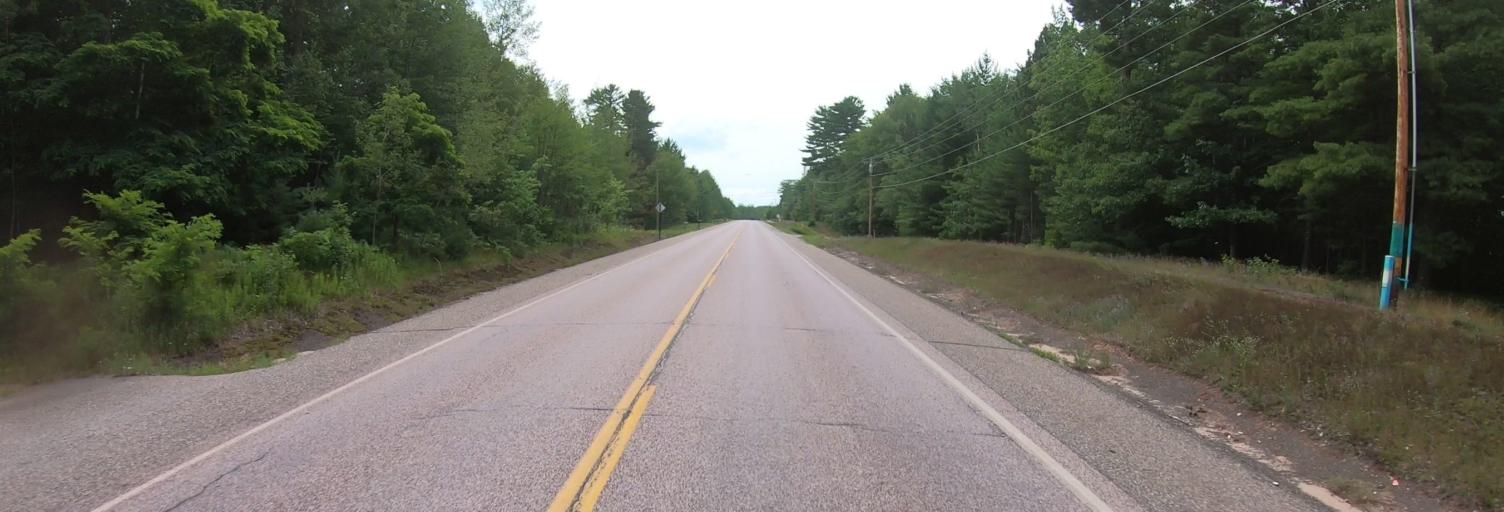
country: US
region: Michigan
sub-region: Marquette County
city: Harvey
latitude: 46.4620
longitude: -87.3887
